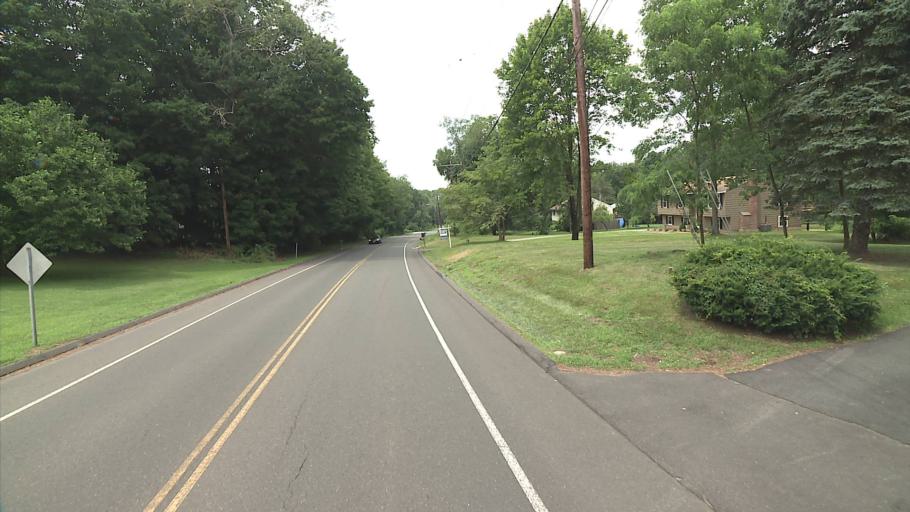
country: US
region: Connecticut
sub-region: New Haven County
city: Madison
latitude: 41.3028
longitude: -72.5887
